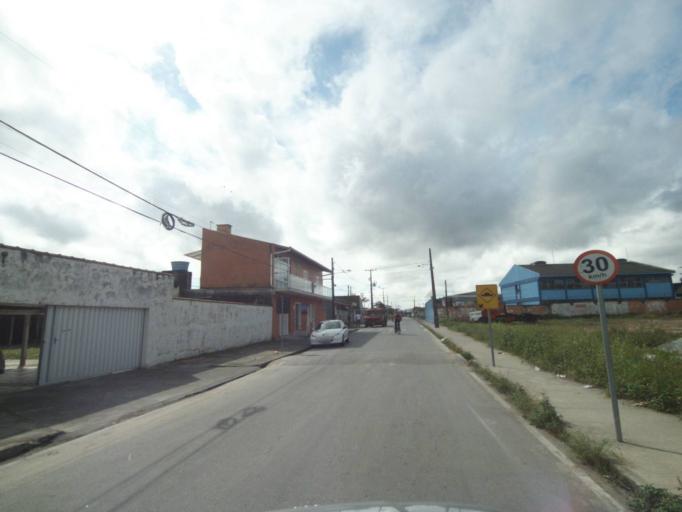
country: BR
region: Parana
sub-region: Paranagua
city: Paranagua
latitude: -25.5677
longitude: -48.5664
